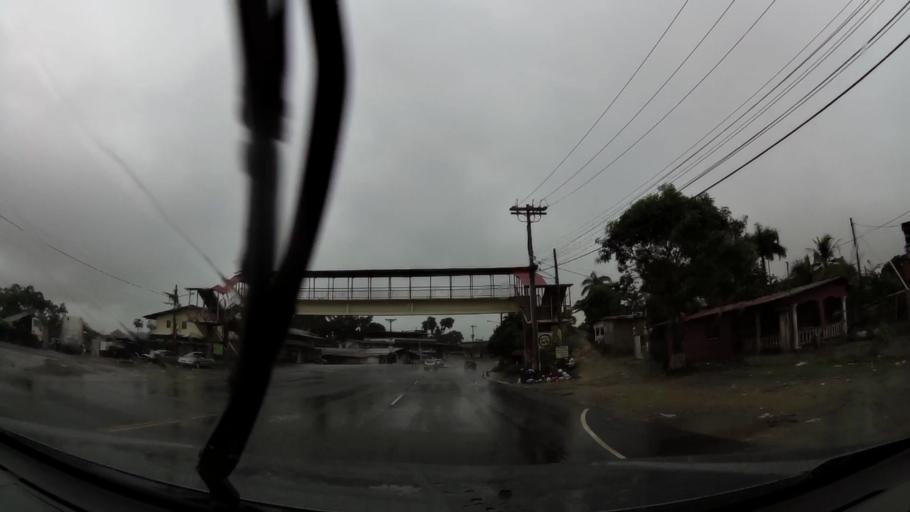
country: PA
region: Colon
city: Santa Rita Arriba
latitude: 9.3321
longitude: -79.8035
